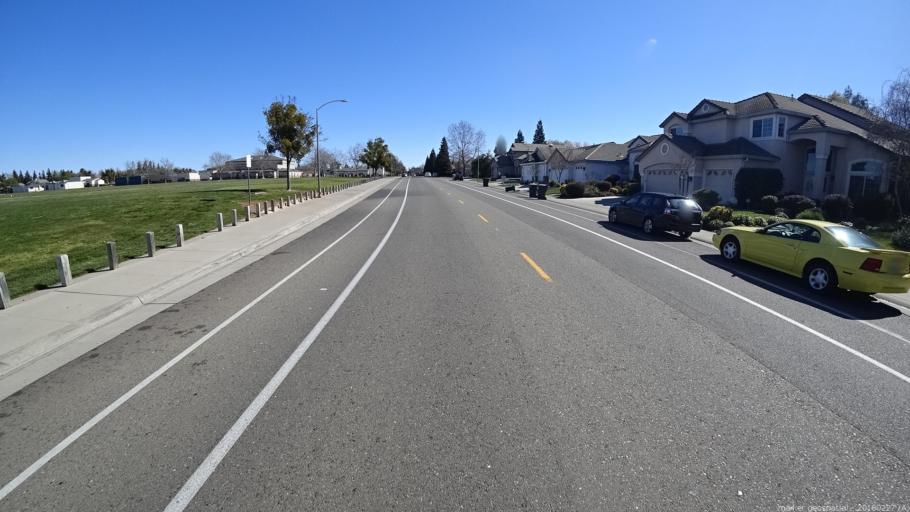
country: US
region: California
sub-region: Sacramento County
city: Antelope
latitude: 38.7172
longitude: -121.3436
